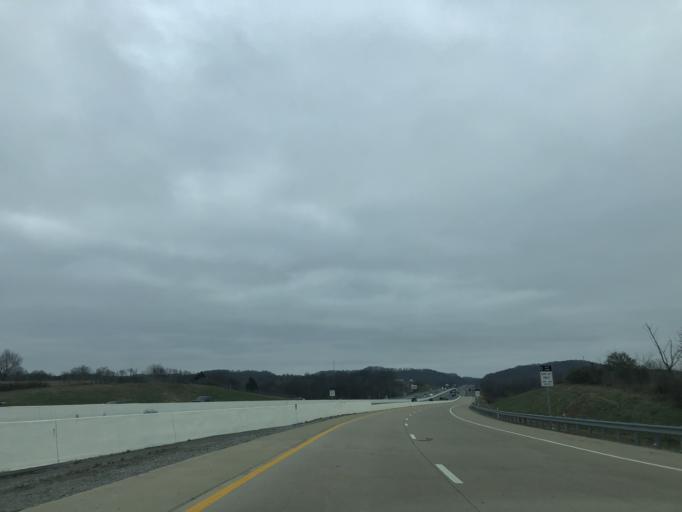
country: US
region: Tennessee
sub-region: Williamson County
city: Franklin
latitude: 35.8577
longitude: -86.8323
